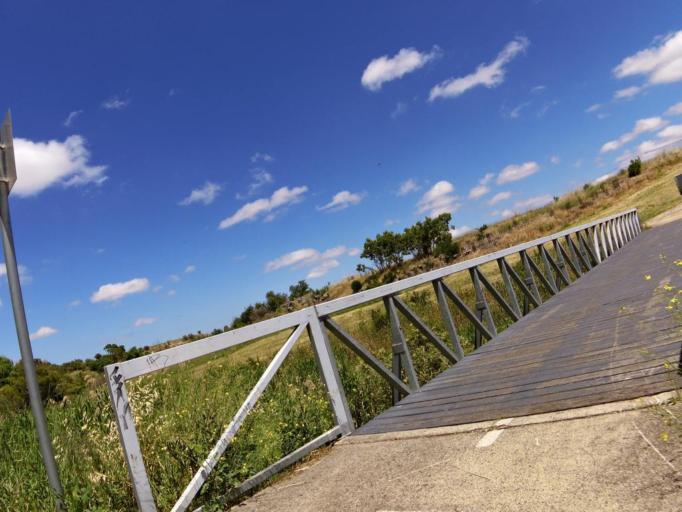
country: AU
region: Victoria
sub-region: Moreland
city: Fawkner
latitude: -37.7115
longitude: 144.9790
